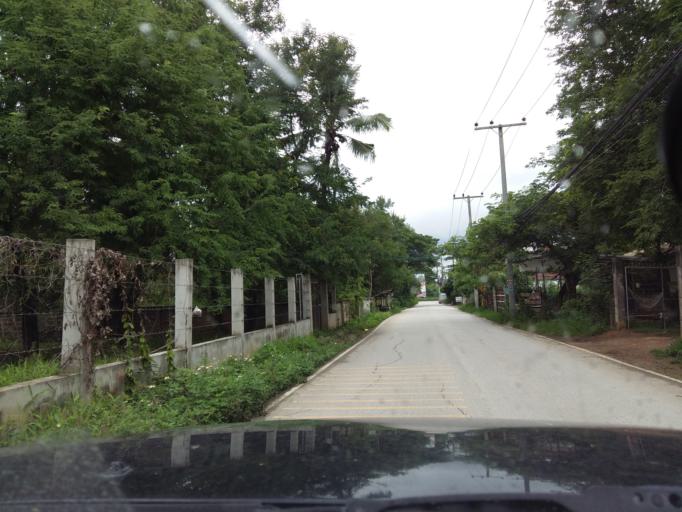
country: TH
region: Chiang Mai
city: Chiang Mai
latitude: 18.7557
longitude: 98.9743
